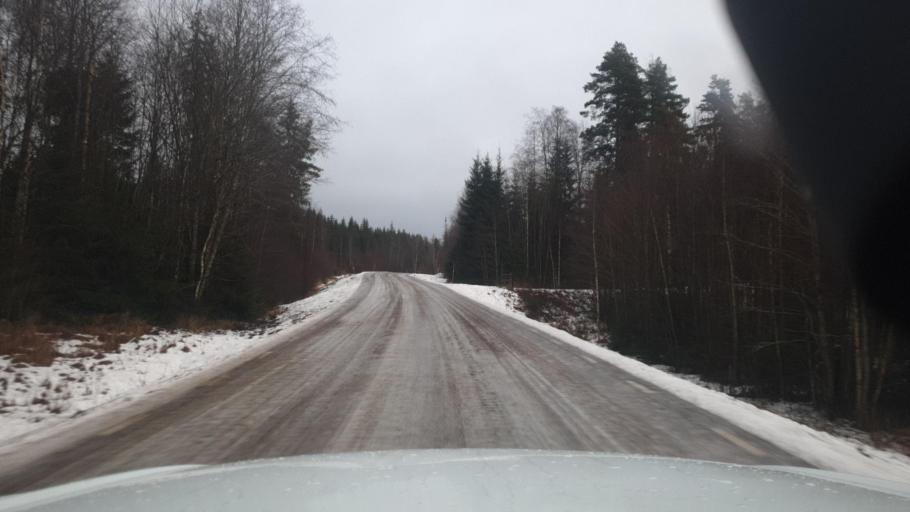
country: SE
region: Vaermland
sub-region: Torsby Kommun
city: Torsby
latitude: 59.9824
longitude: 12.8231
